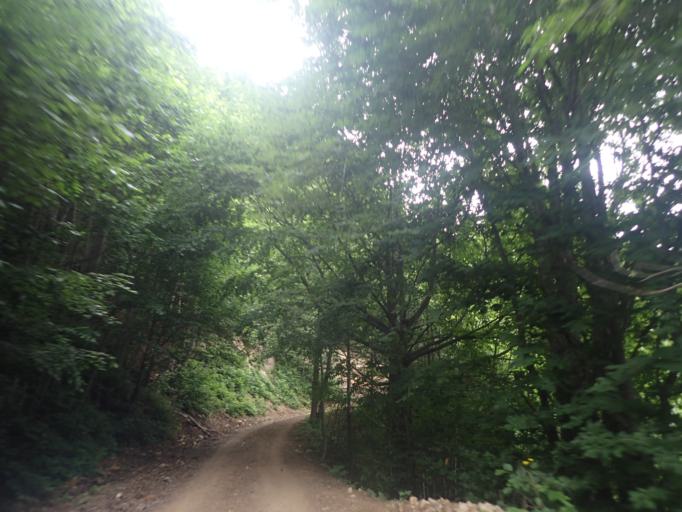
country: TR
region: Ordu
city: Akkus
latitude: 40.8652
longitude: 37.0061
